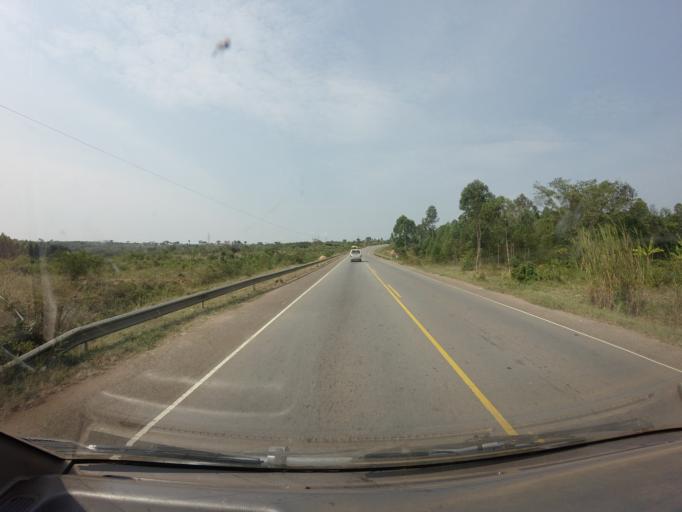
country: UG
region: Central Region
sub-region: Lwengo District
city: Lwengo
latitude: -0.3990
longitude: 31.3969
